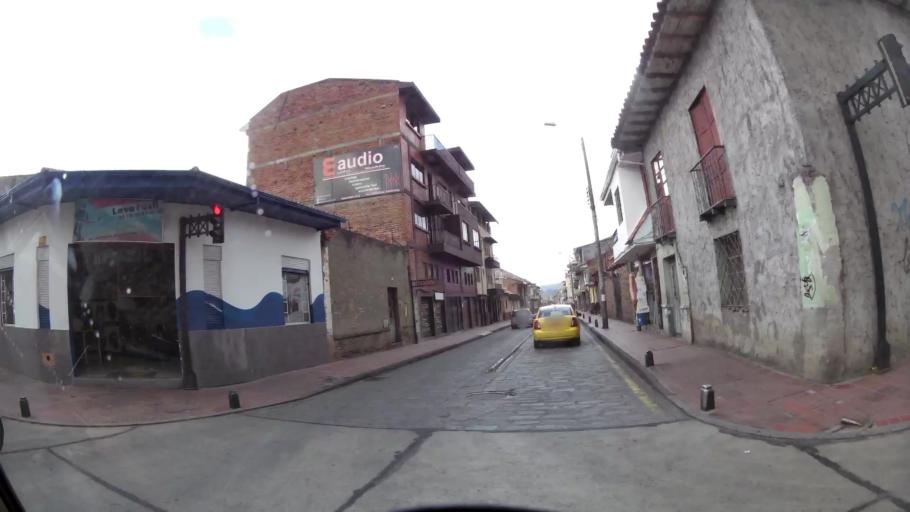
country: EC
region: Azuay
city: Cuenca
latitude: -2.8920
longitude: -79.0112
